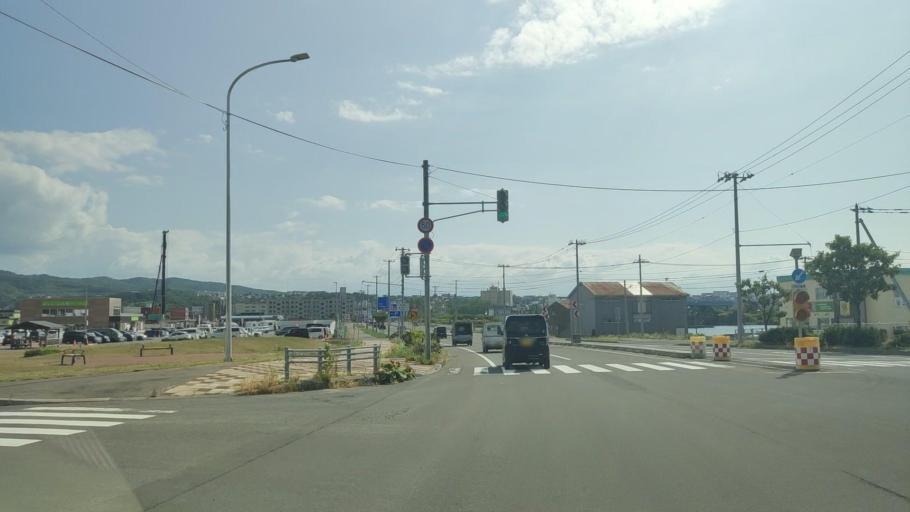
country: JP
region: Hokkaido
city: Rumoi
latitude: 43.9460
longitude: 141.6487
